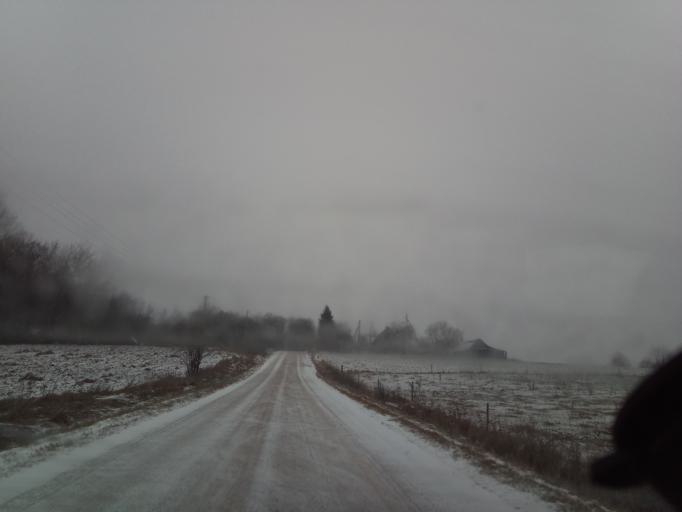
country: LT
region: Utenos apskritis
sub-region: Anyksciai
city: Anyksciai
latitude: 55.4421
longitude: 25.1039
